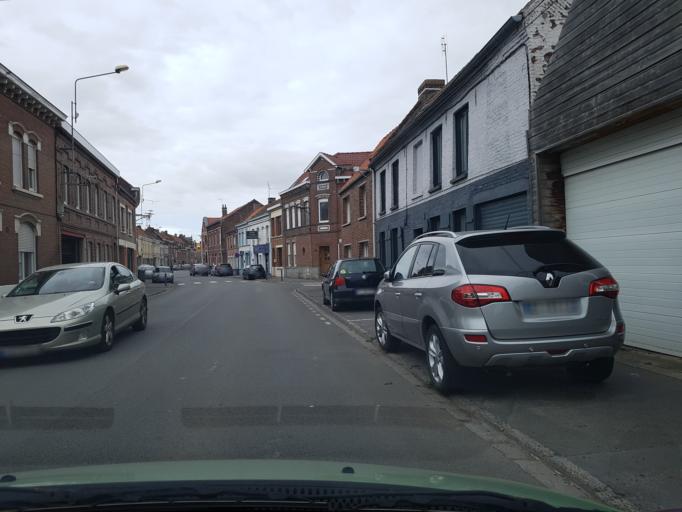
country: FR
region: Nord-Pas-de-Calais
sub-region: Departement du Nord
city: Annoeullin
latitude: 50.5242
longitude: 2.9364
